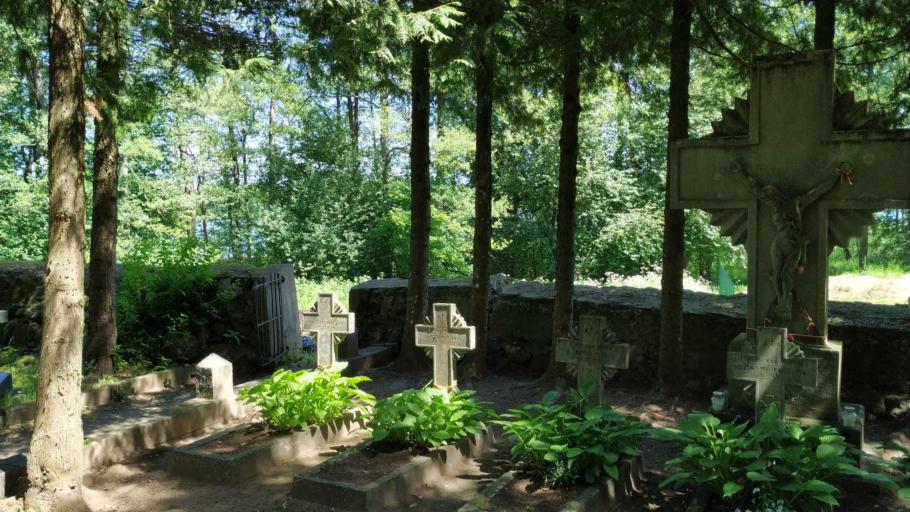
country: LT
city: Moletai
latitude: 55.0756
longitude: 25.2624
